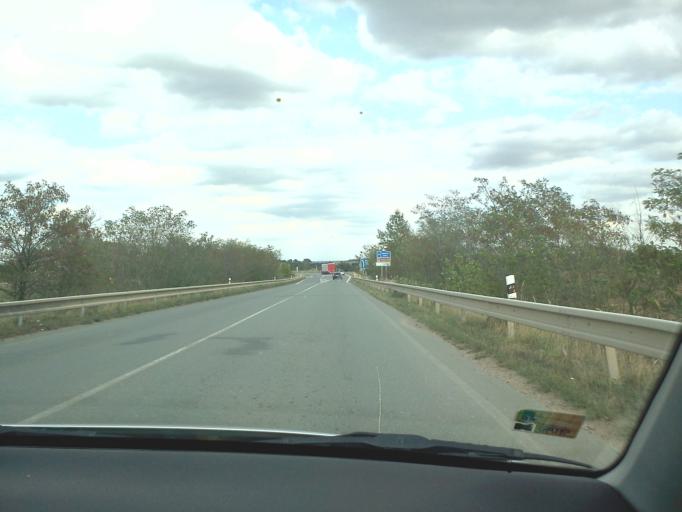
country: CZ
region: Central Bohemia
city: Lysa nad Labem
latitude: 50.1779
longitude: 14.8563
